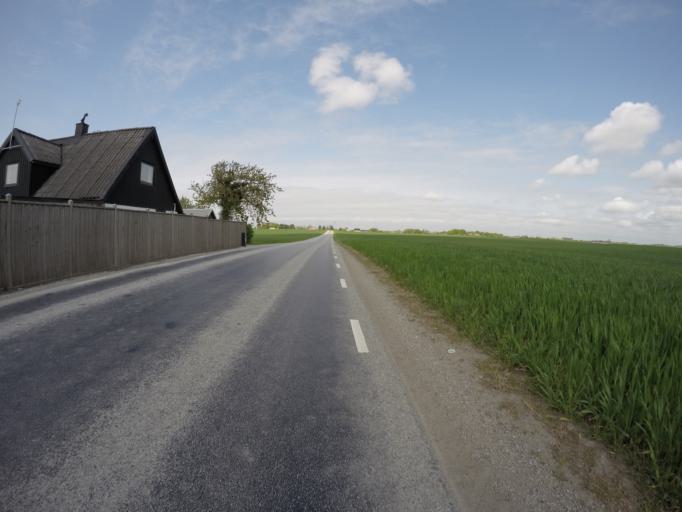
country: SE
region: Skane
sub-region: Malmo
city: Tygelsjo
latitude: 55.5357
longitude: 13.0303
